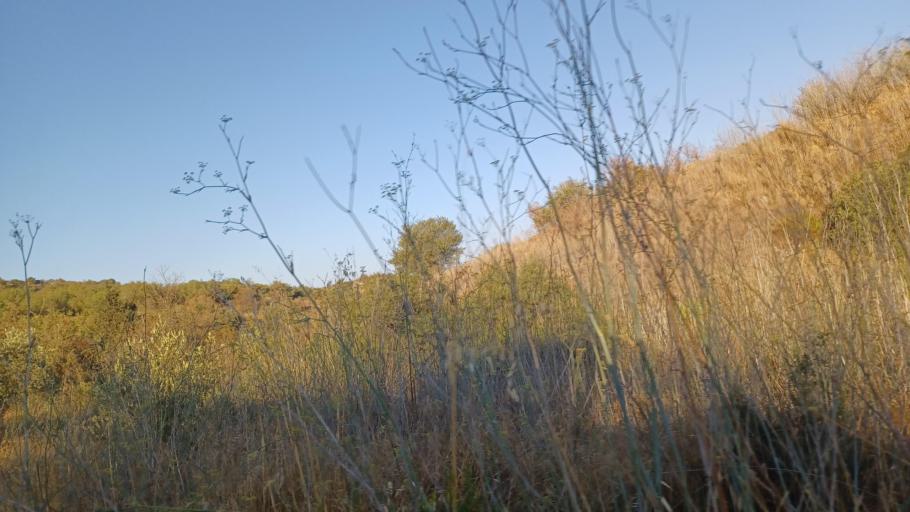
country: CY
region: Pafos
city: Mesogi
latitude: 34.9091
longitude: 32.5241
